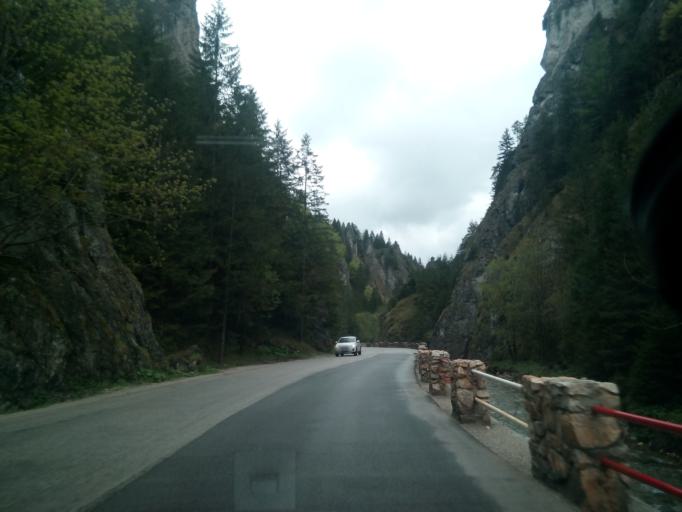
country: SK
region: Zilinsky
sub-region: Okres Zilina
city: Terchova
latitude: 49.2426
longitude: 19.0385
